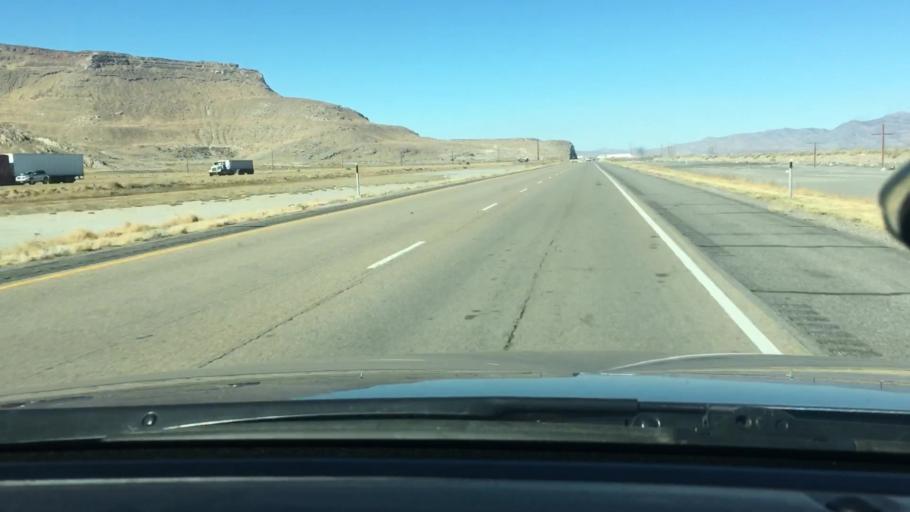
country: US
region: Utah
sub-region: Tooele County
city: Grantsville
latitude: 40.7385
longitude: -112.6164
